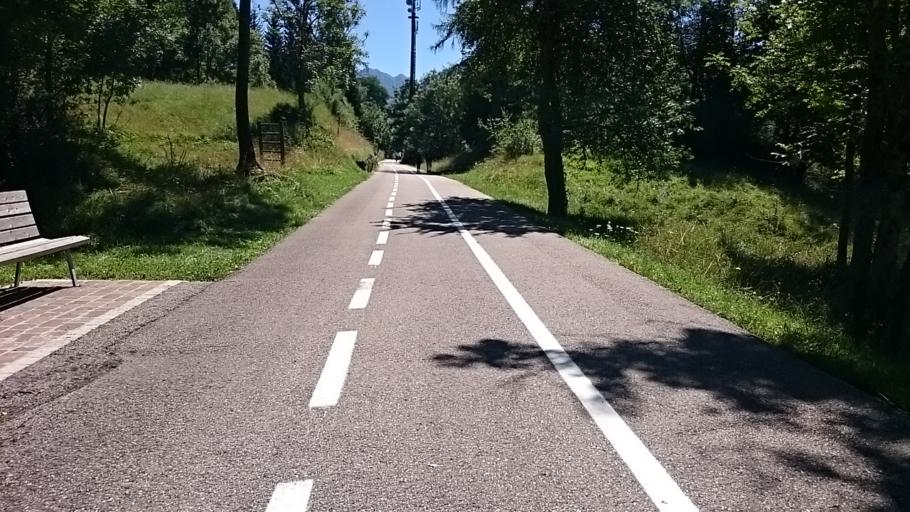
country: IT
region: Veneto
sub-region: Provincia di Belluno
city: Borca
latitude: 46.4401
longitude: 12.2170
